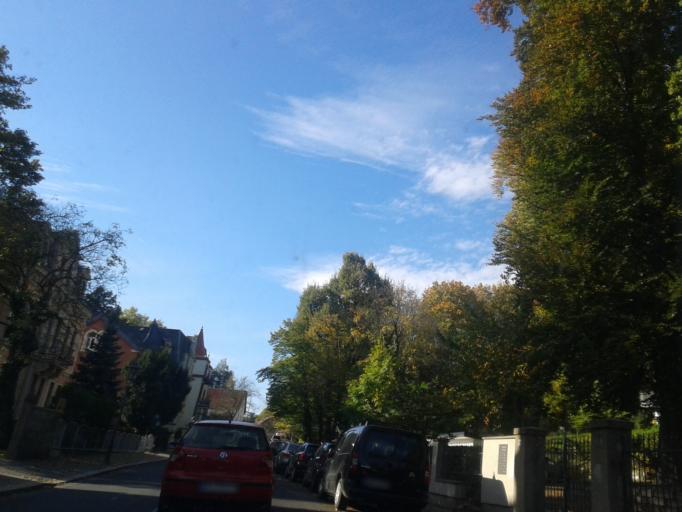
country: DE
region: Saxony
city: Albertstadt
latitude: 51.0961
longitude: 13.7222
